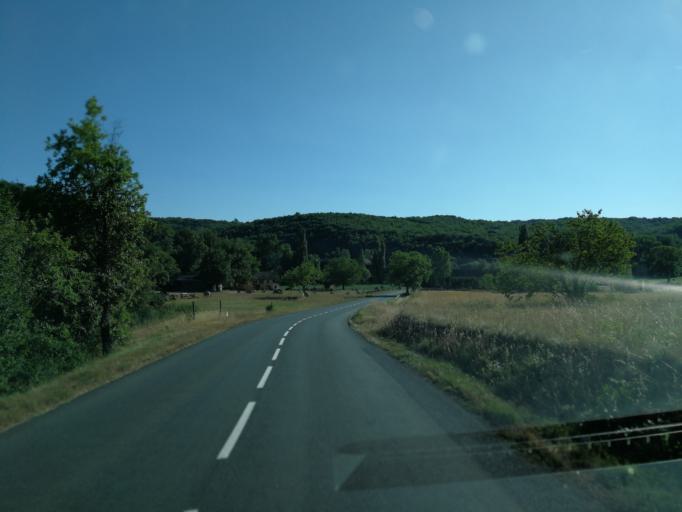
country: FR
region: Midi-Pyrenees
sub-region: Departement du Lot
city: Salviac
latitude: 44.7089
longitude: 1.2988
